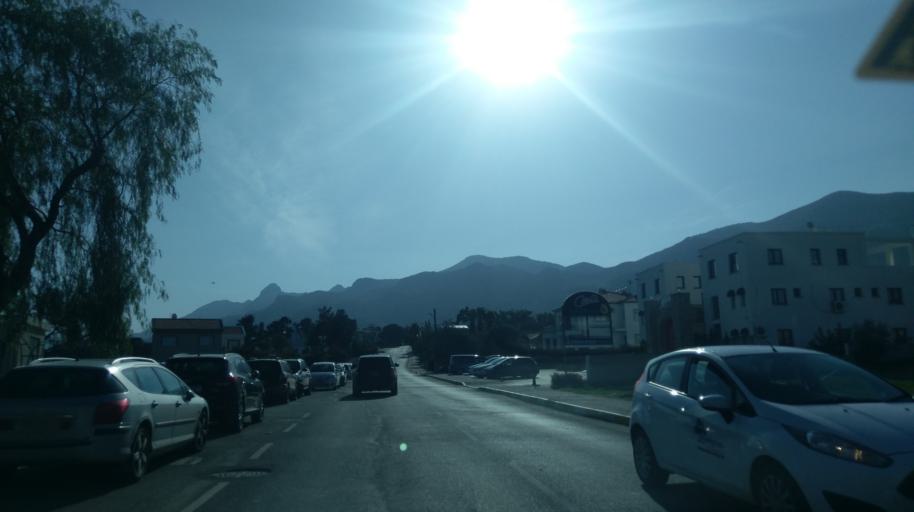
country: CY
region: Keryneia
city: Kyrenia
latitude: 35.3244
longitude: 33.3449
